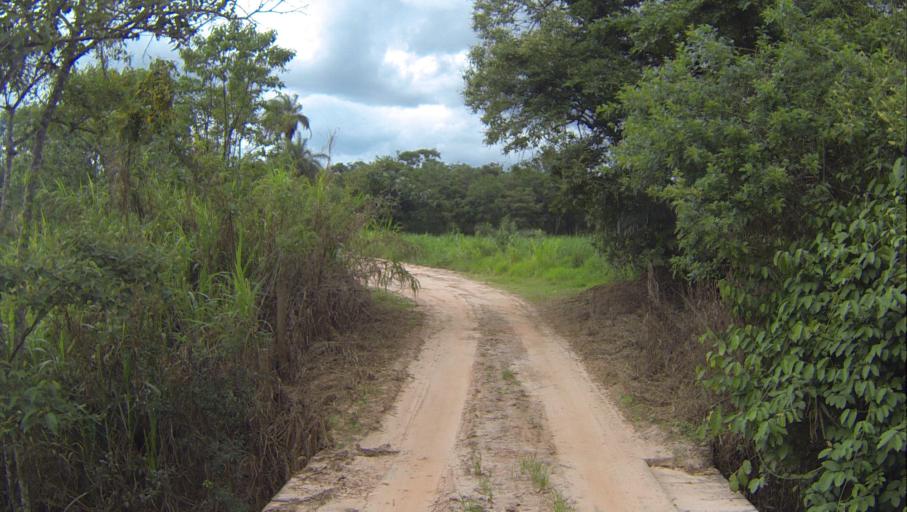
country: BR
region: Minas Gerais
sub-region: Brumadinho
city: Brumadinho
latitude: -20.1600
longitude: -44.1302
